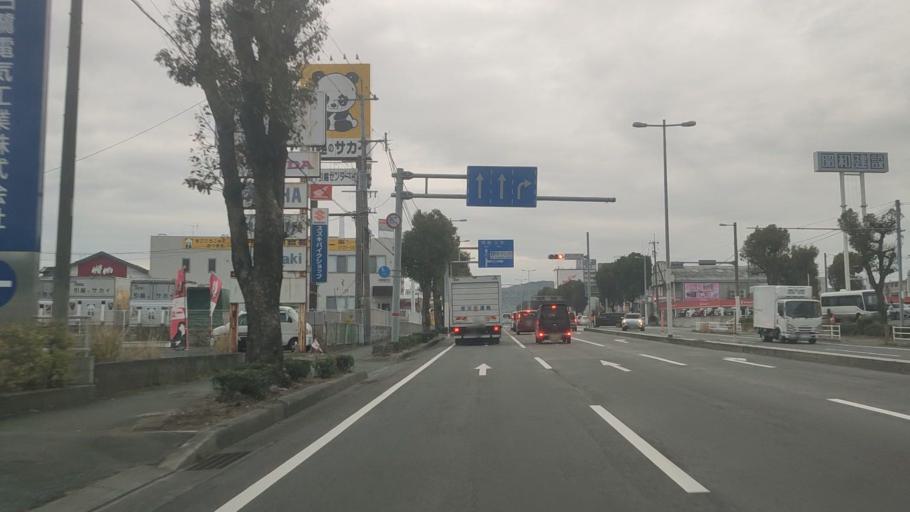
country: JP
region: Kumamoto
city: Kumamoto
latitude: 32.8297
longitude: 130.7703
